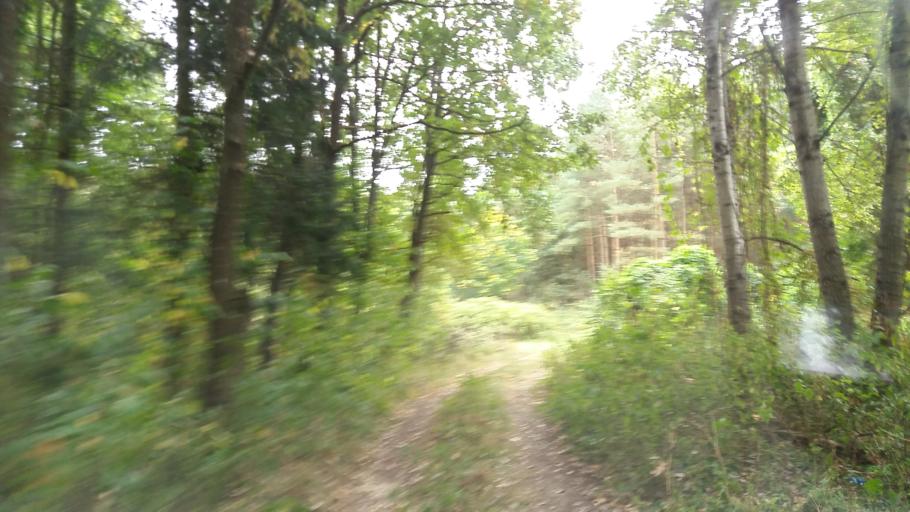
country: PL
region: West Pomeranian Voivodeship
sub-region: Powiat choszczenski
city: Krzecin
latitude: 52.9964
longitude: 15.5519
